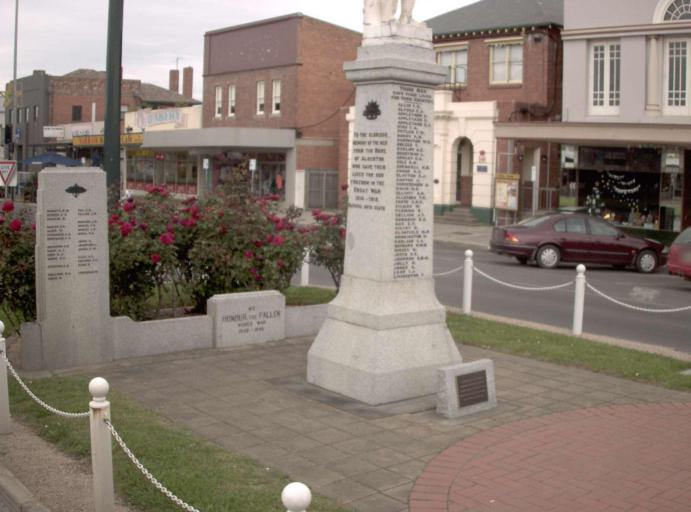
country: AU
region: Victoria
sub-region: Latrobe
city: Traralgon
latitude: -38.5624
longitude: 146.6763
